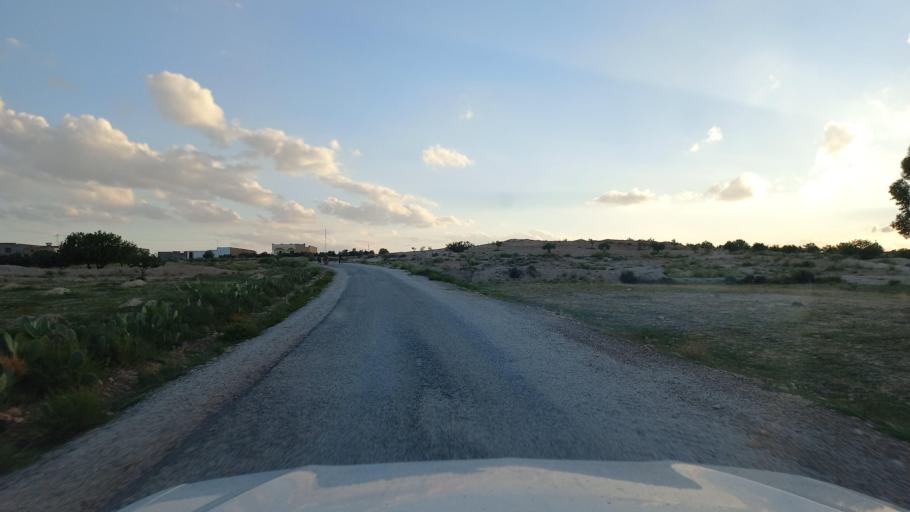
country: TN
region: Al Qasrayn
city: Sbiba
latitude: 35.3748
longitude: 9.0624
